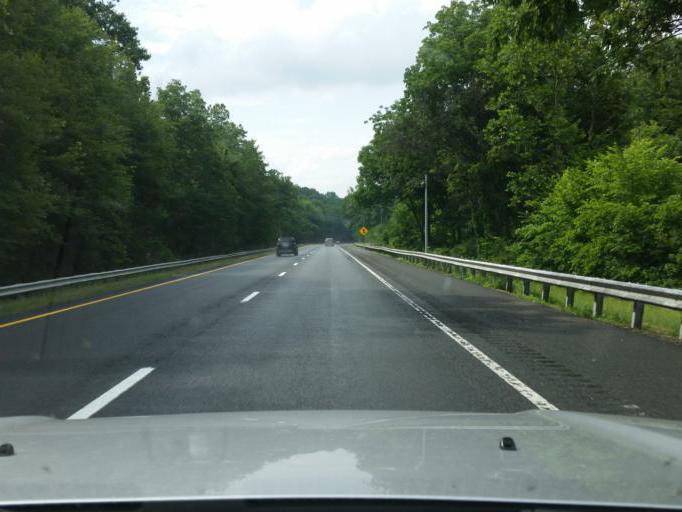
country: US
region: Maryland
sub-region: Montgomery County
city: Clarksburg
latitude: 39.2635
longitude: -77.3104
